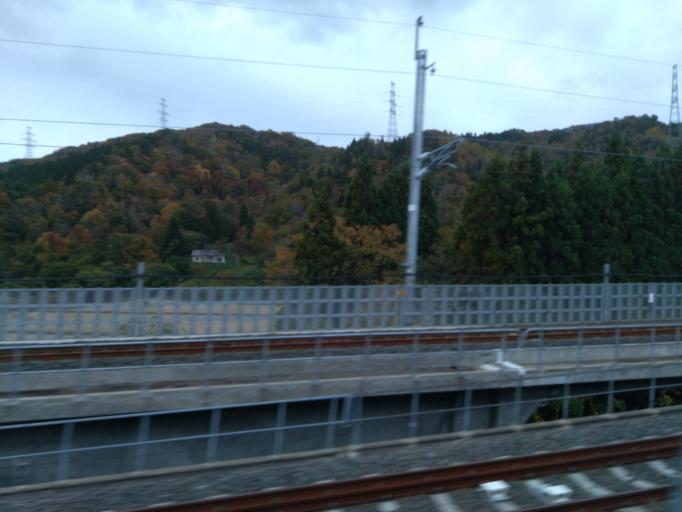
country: JP
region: Aomori
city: Goshogawara
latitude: 41.1485
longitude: 140.5125
